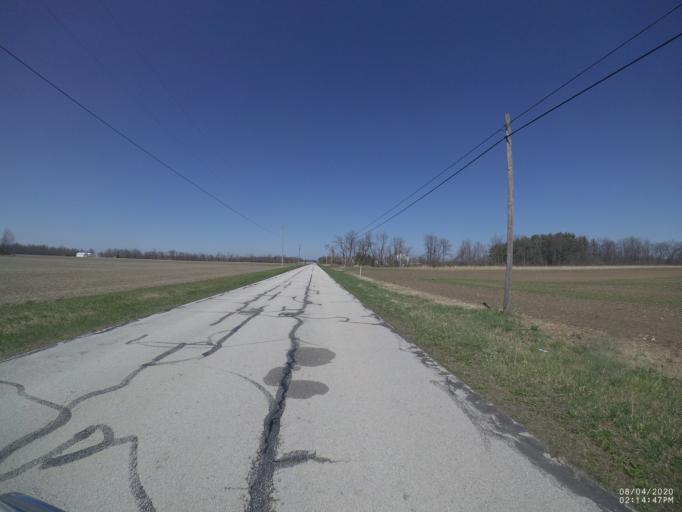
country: US
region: Ohio
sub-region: Sandusky County
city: Gibsonburg
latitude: 41.2740
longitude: -83.2643
